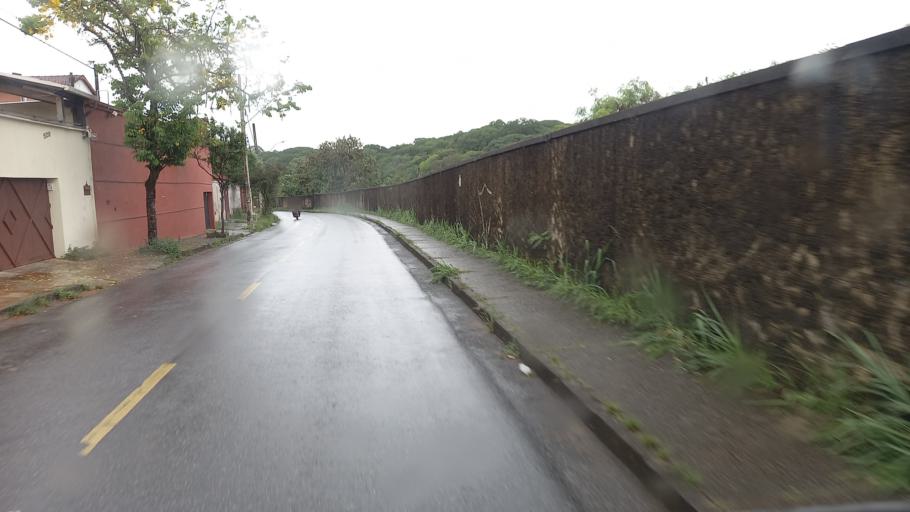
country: BR
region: Minas Gerais
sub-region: Belo Horizonte
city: Belo Horizonte
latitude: -19.8893
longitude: -43.9115
